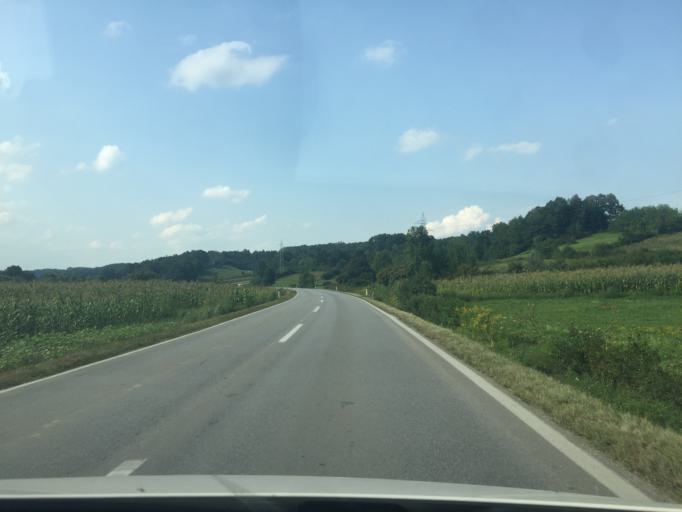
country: BA
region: Federation of Bosnia and Herzegovina
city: Mionica
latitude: 44.8067
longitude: 18.4763
